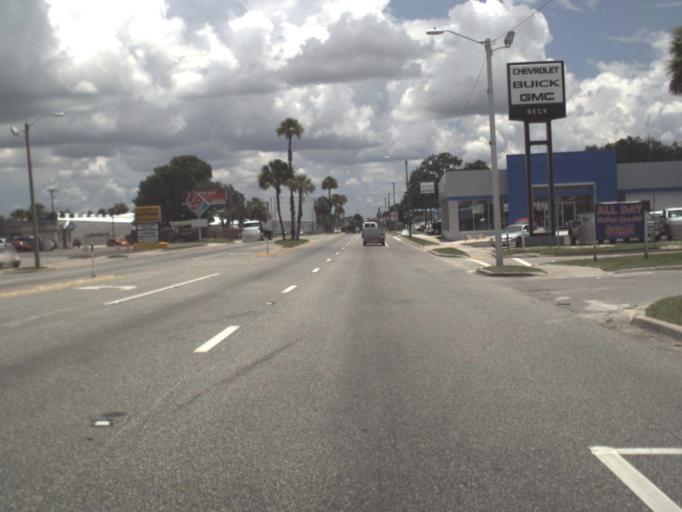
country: US
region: Florida
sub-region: Putnam County
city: Palatka
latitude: 29.6498
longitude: -81.6471
